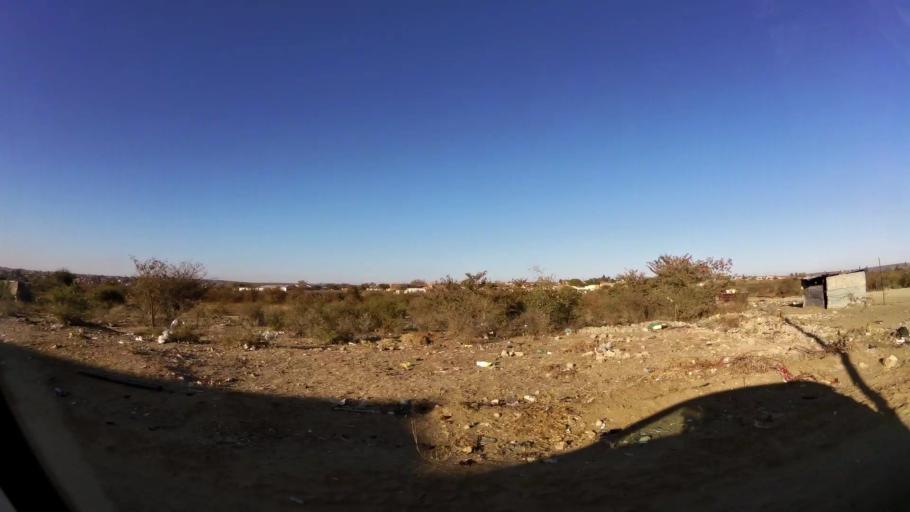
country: ZA
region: Limpopo
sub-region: Capricorn District Municipality
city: Polokwane
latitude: -23.8407
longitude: 29.3602
